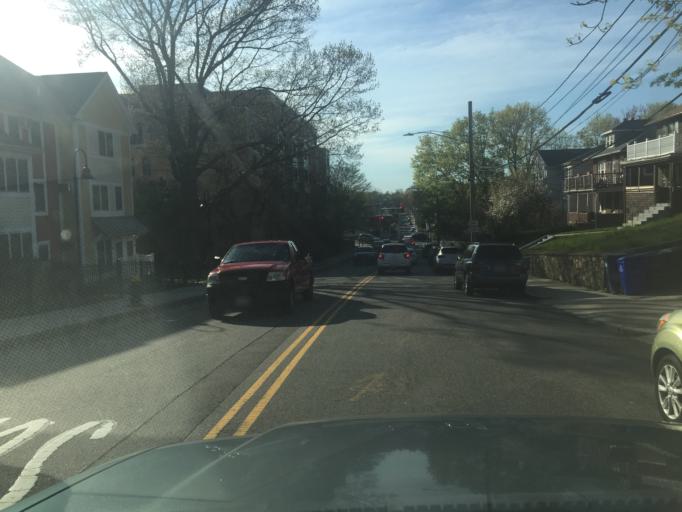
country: US
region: Massachusetts
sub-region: Suffolk County
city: Jamaica Plain
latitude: 42.2776
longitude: -71.1360
